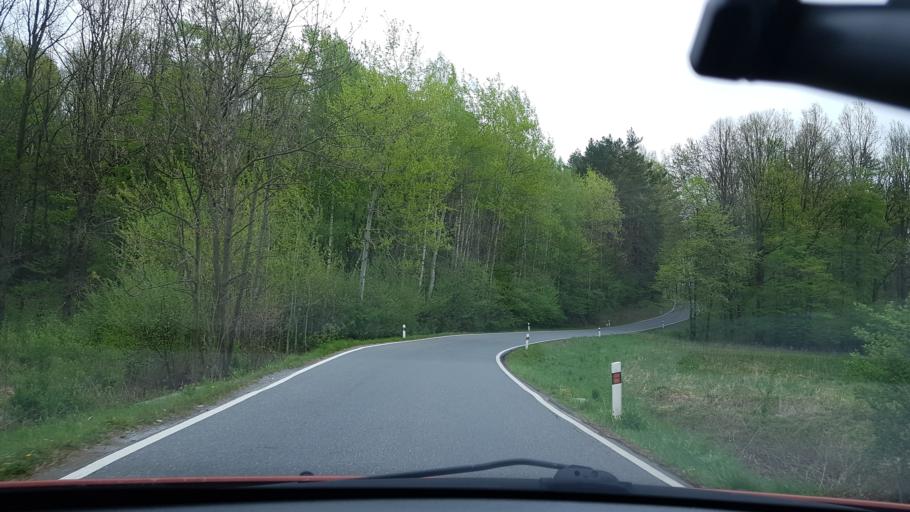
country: CZ
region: Olomoucky
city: Vidnava
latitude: 50.3613
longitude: 17.2067
